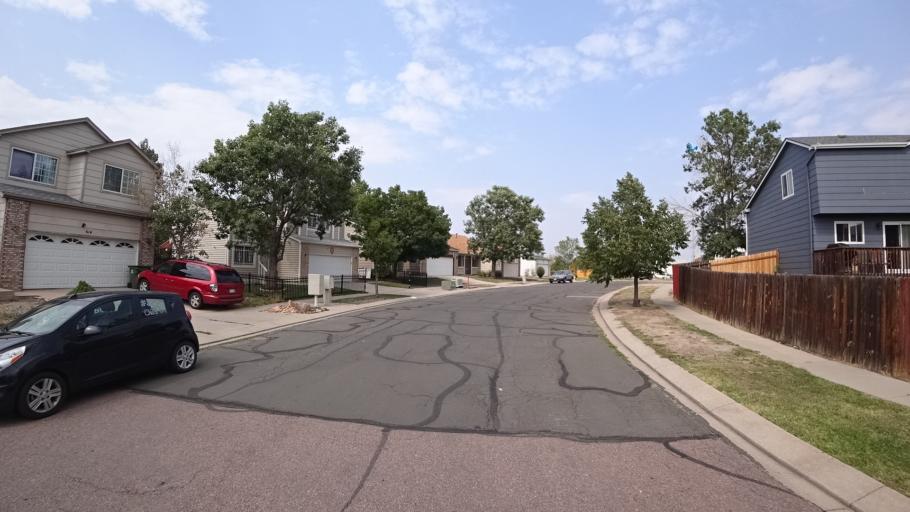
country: US
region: Colorado
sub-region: El Paso County
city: Stratmoor
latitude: 38.8232
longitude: -104.7470
